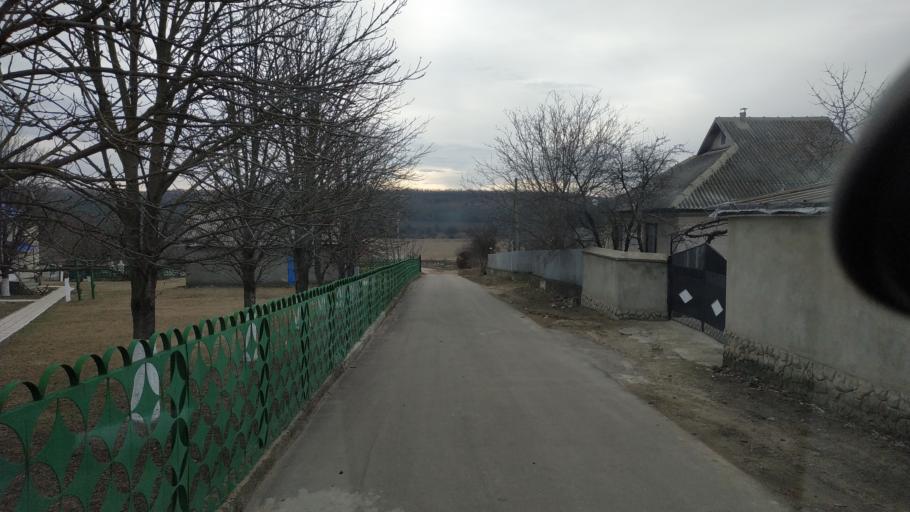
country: MD
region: Telenesti
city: Cocieri
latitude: 47.2552
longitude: 29.0615
